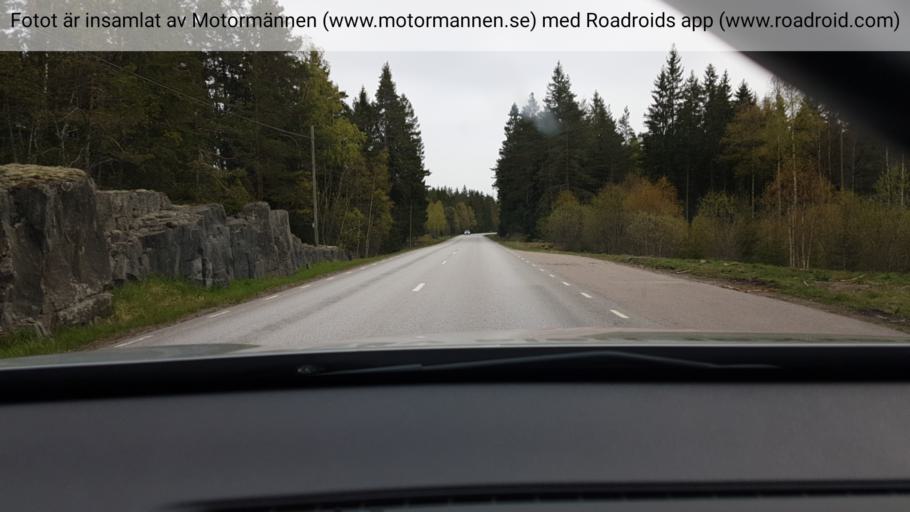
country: SE
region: Stockholm
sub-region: Sigtuna Kommun
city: Marsta
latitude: 59.7915
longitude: 18.0386
